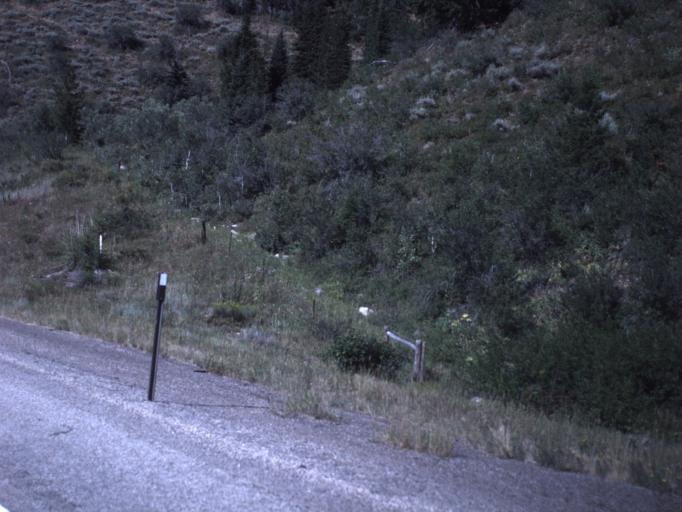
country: US
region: Utah
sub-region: Wasatch County
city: Heber
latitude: 40.3369
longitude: -111.2610
